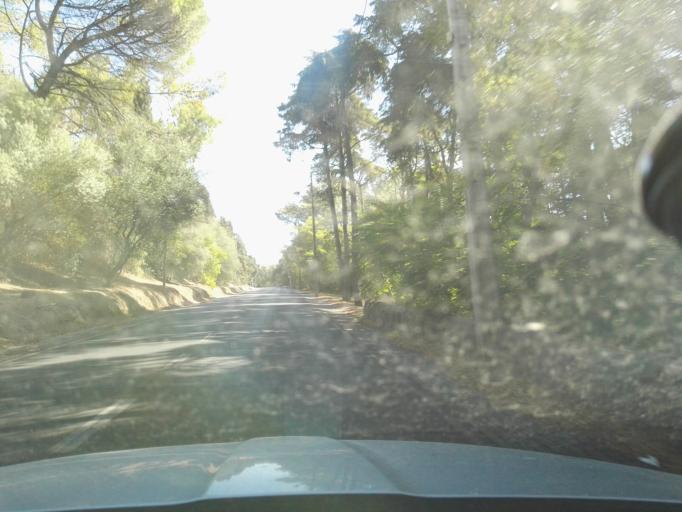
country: PT
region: Lisbon
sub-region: Odivelas
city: Pontinha
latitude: 38.7304
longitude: -9.1980
